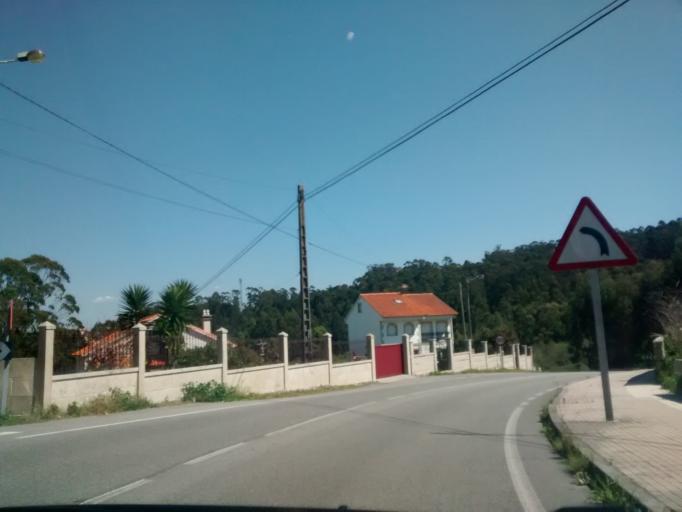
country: ES
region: Galicia
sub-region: Provincia de Pontevedra
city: O Grove
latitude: 42.4849
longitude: -8.8747
